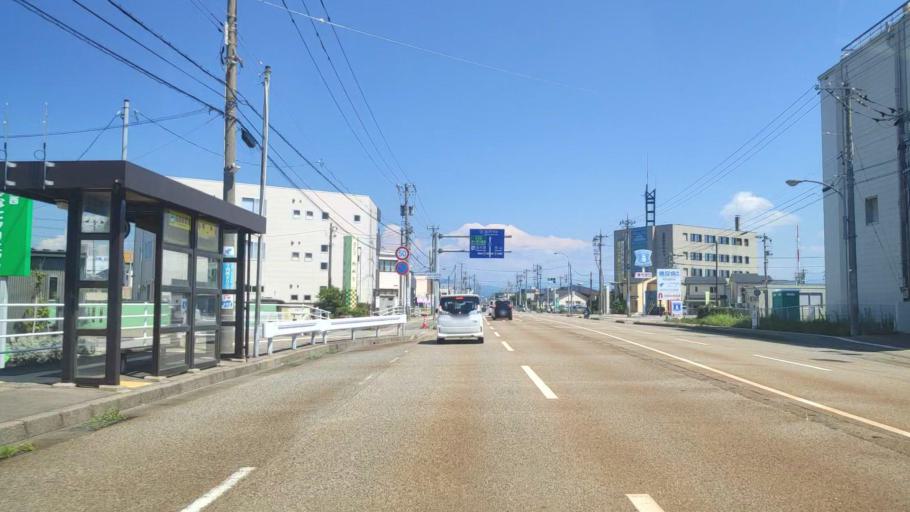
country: JP
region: Ishikawa
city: Kanazawa-shi
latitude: 36.5993
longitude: 136.5973
